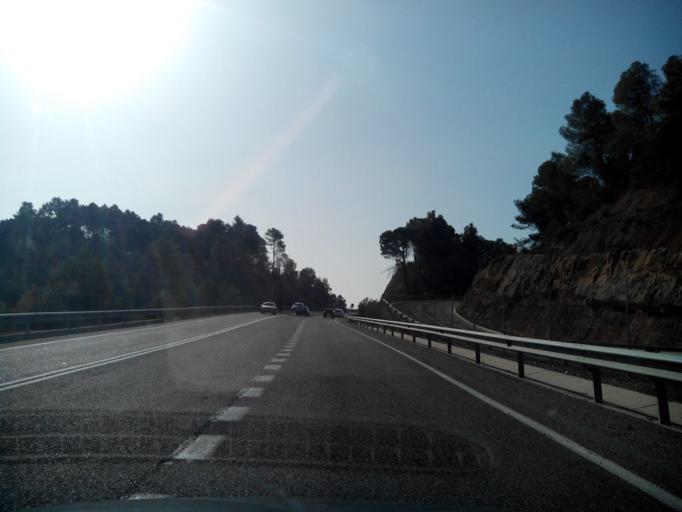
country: ES
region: Catalonia
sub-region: Provincia de Barcelona
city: Castellfollit del Boix
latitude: 41.6515
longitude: 1.7063
